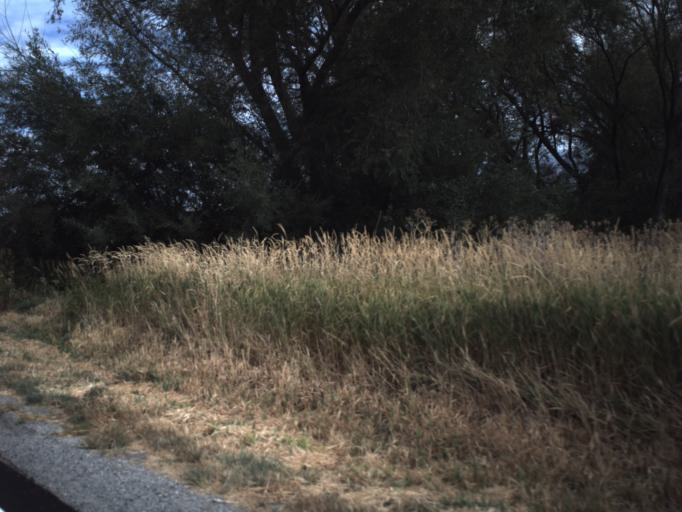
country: US
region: Utah
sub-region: Cache County
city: Mendon
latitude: 41.7440
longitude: -111.9793
